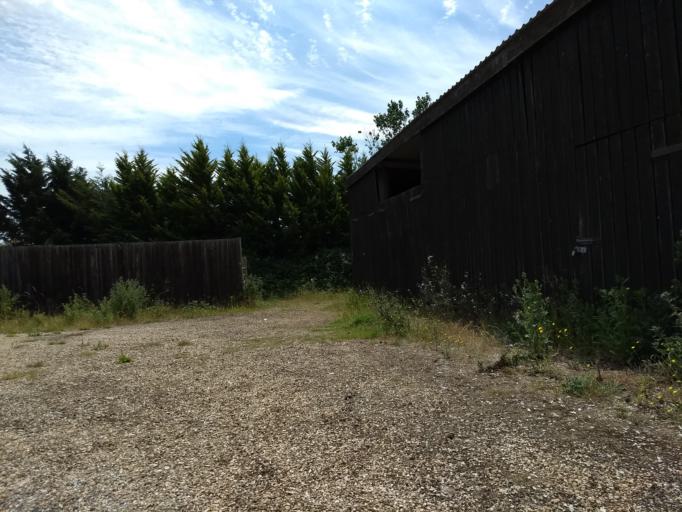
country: GB
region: England
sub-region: Isle of Wight
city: Newport
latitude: 50.7026
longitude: -1.3147
